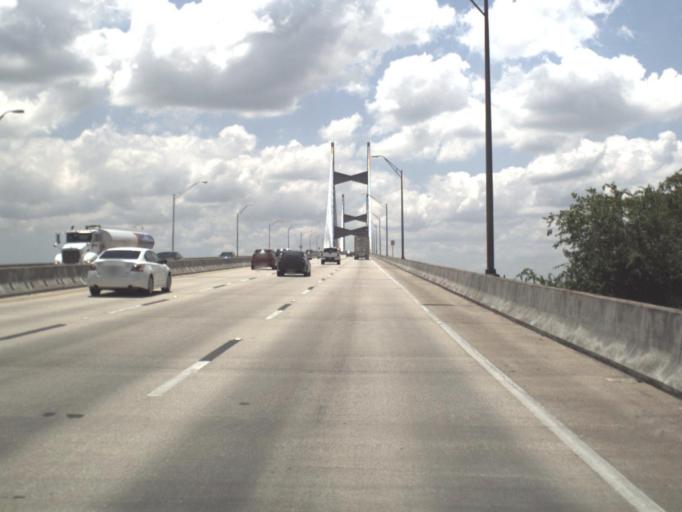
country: US
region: Florida
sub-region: Duval County
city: Jacksonville
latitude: 30.3930
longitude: -81.5607
